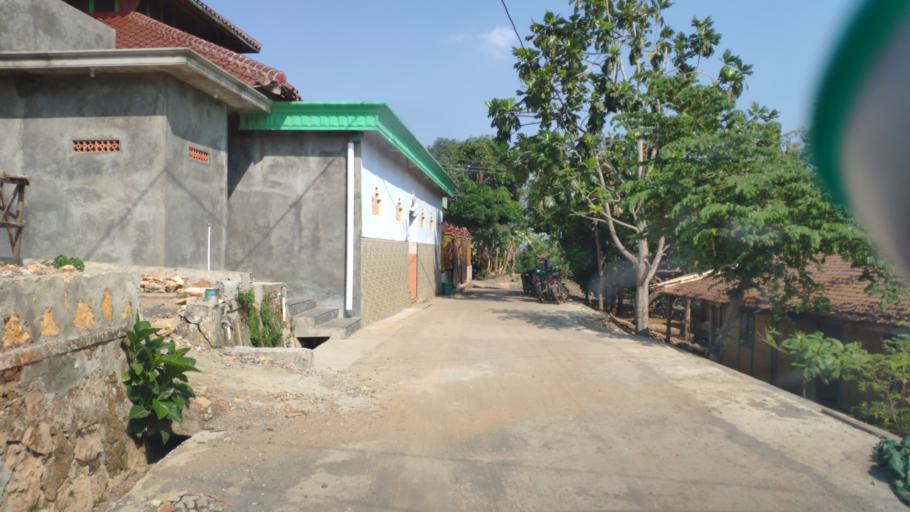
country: ID
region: Central Java
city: Ngapus
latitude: -6.9387
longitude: 111.2086
